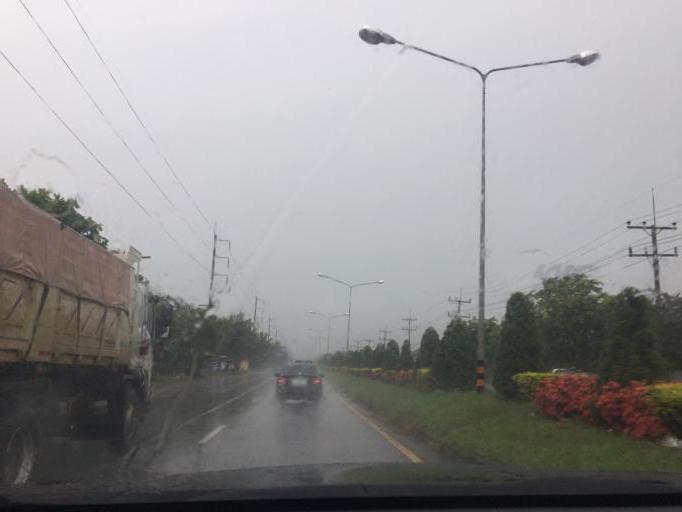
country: TH
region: Chiang Rai
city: Mae Fa Luang
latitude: 20.2359
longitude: 99.8562
